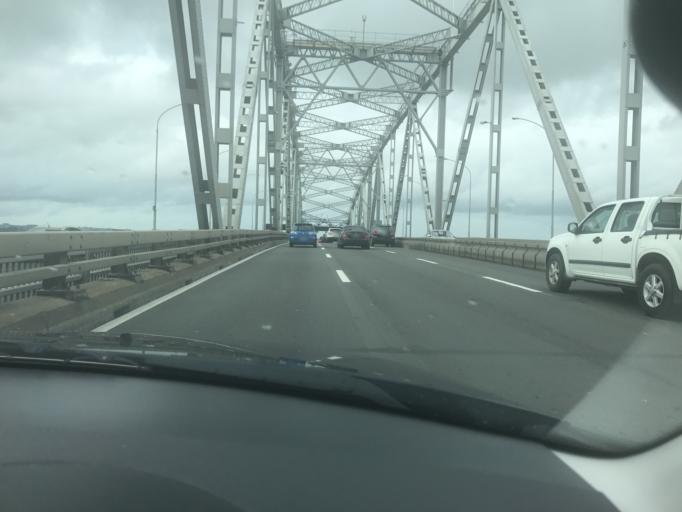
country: NZ
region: Auckland
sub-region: Auckland
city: North Shore
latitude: -36.8298
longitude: 174.7462
